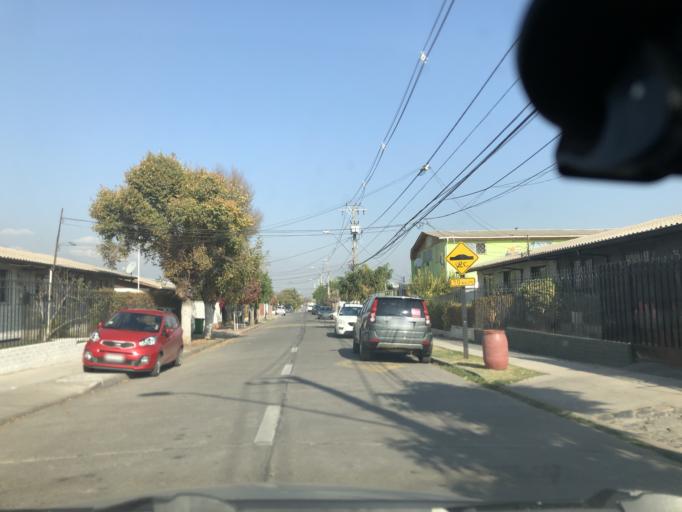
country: CL
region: Santiago Metropolitan
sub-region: Provincia de Cordillera
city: Puente Alto
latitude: -33.6115
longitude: -70.5615
